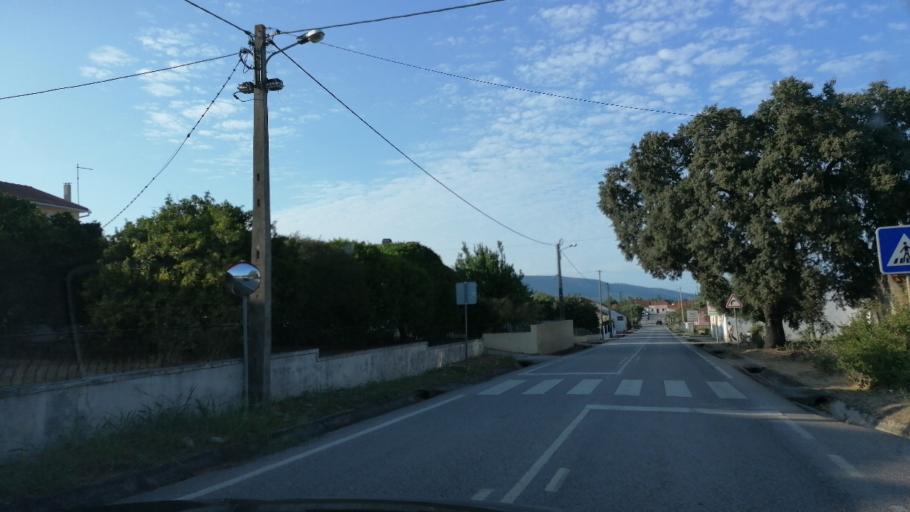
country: PT
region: Santarem
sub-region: Alcanena
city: Alcanena
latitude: 39.4484
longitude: -8.6228
